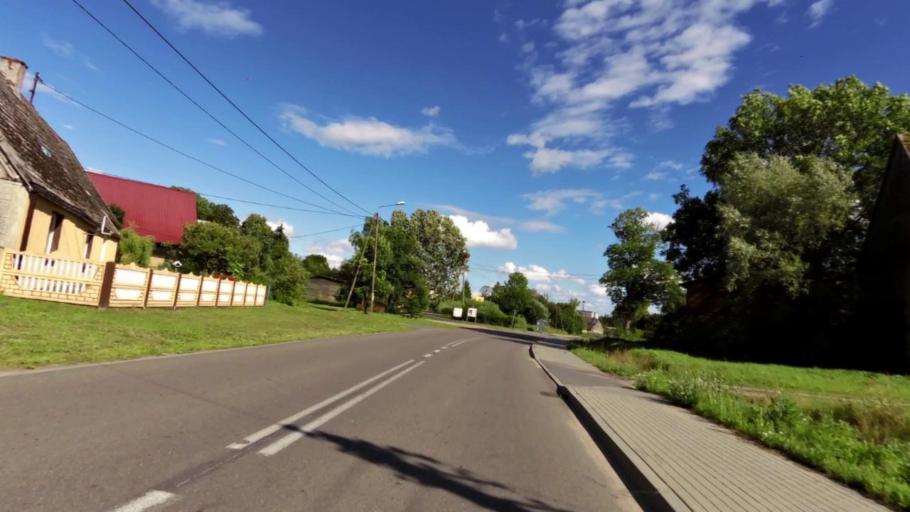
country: PL
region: West Pomeranian Voivodeship
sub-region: Powiat slawienski
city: Slawno
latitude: 54.4597
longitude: 16.7356
